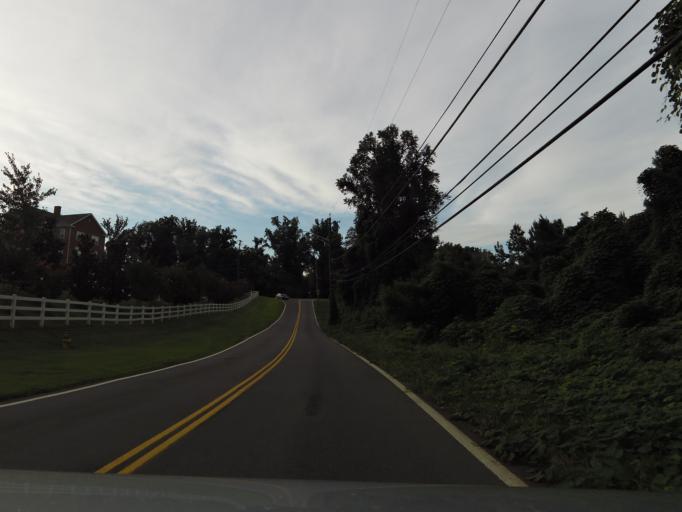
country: US
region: Tennessee
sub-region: Knox County
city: Knoxville
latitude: 35.9329
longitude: -83.9313
